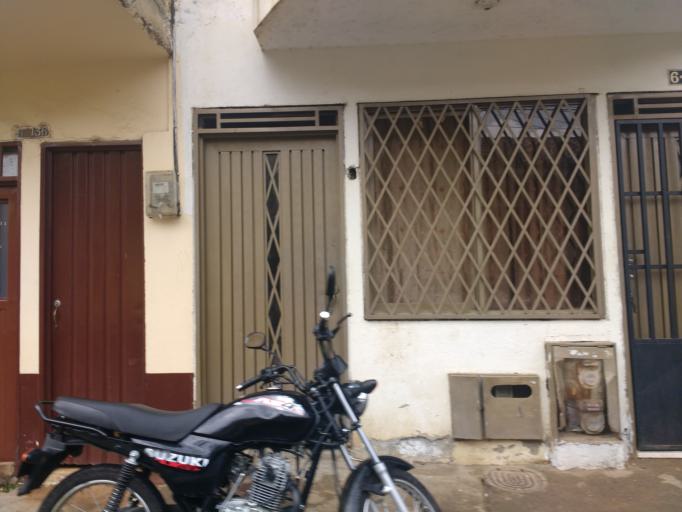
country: CO
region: Cauca
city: Santander de Quilichao
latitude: 3.0030
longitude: -76.4810
